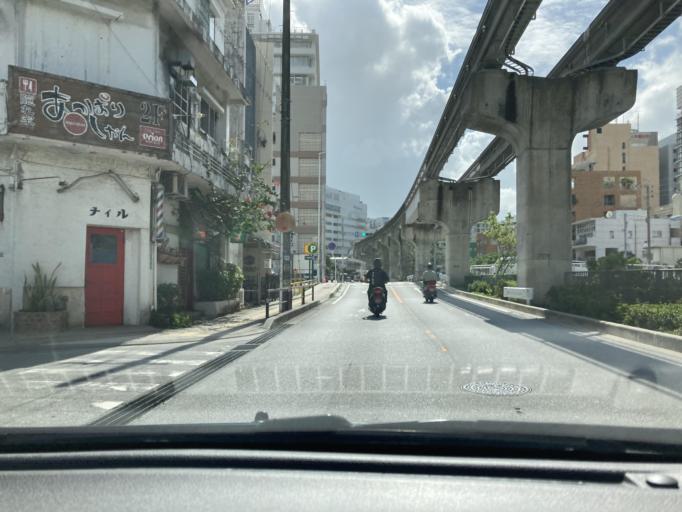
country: JP
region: Okinawa
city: Naha-shi
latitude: 26.2162
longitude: 127.6811
